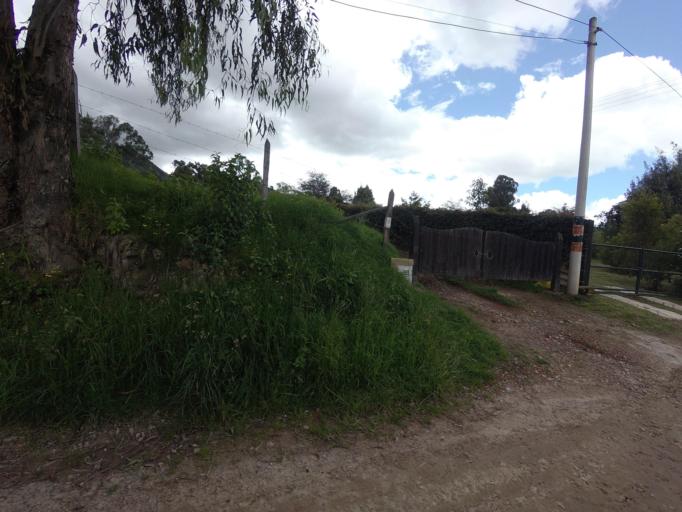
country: CO
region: Cundinamarca
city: Tabio
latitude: 4.9554
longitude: -74.0823
